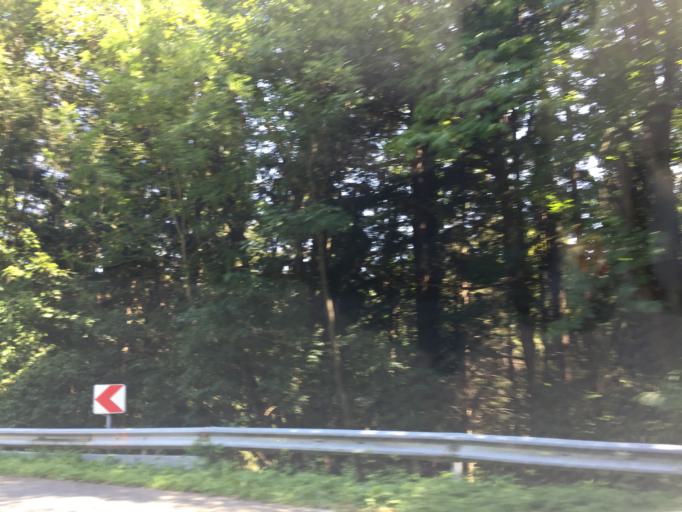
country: SI
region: Trbovlje
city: Trbovlje
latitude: 46.1909
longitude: 15.0673
